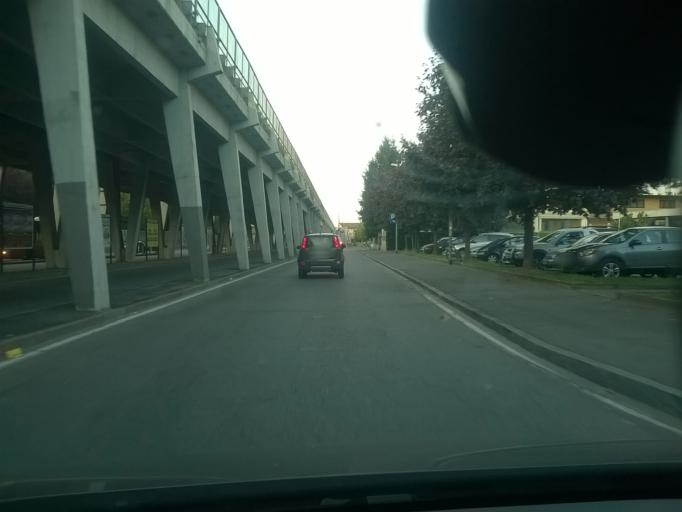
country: IT
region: Lombardy
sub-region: Provincia di Bergamo
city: Orio al Serio
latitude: 45.6934
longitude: 9.6924
